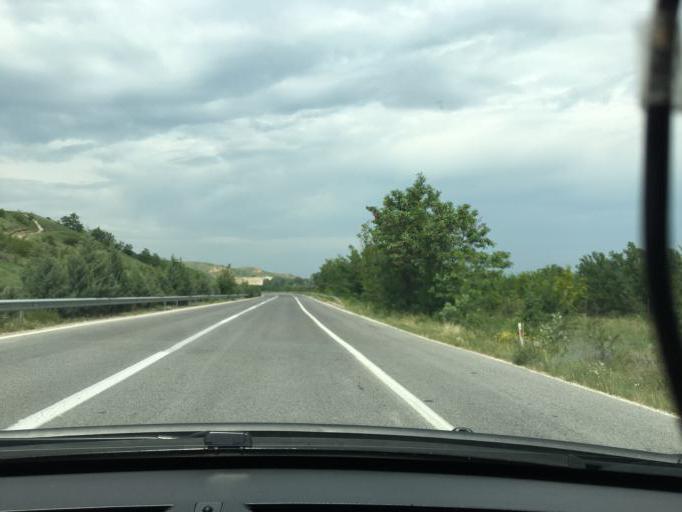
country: MK
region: Demir Kapija
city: Demir Kapija
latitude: 41.4203
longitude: 22.1935
